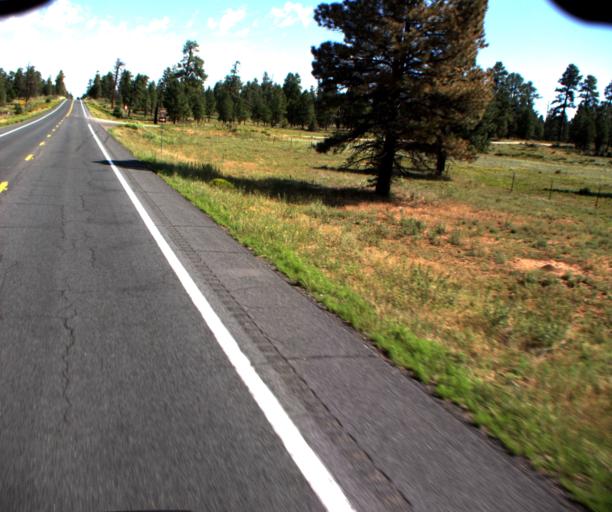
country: US
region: Arizona
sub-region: Coconino County
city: Grand Canyon Village
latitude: 35.9254
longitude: -112.1304
